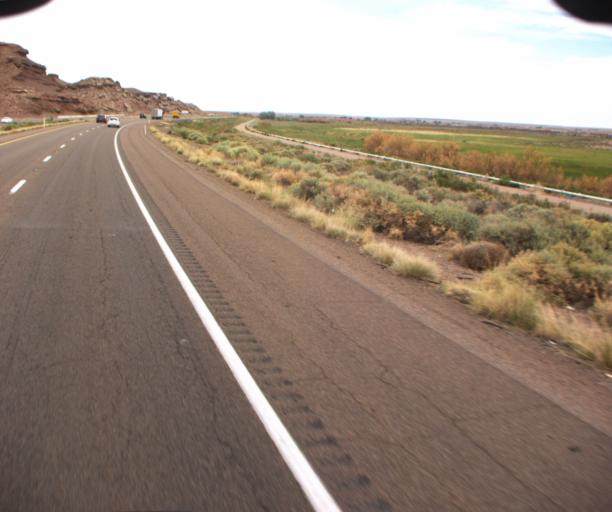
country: US
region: Arizona
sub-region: Navajo County
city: Joseph City
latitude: 34.9397
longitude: -110.2808
